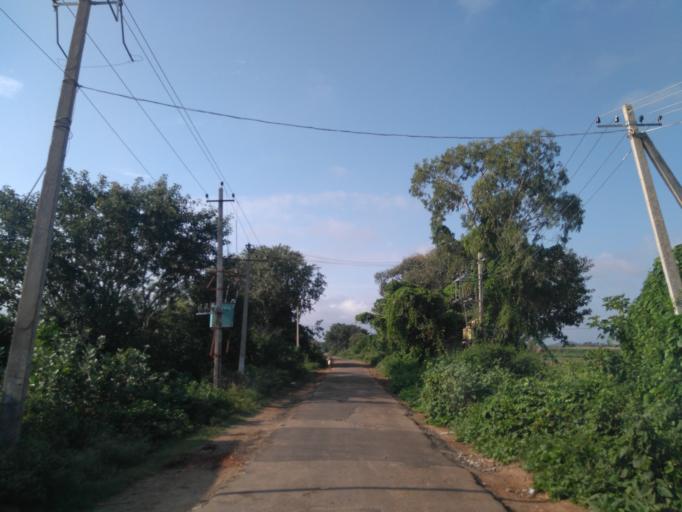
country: IN
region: Karnataka
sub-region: Mandya
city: Malavalli
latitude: 12.2699
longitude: 77.0654
